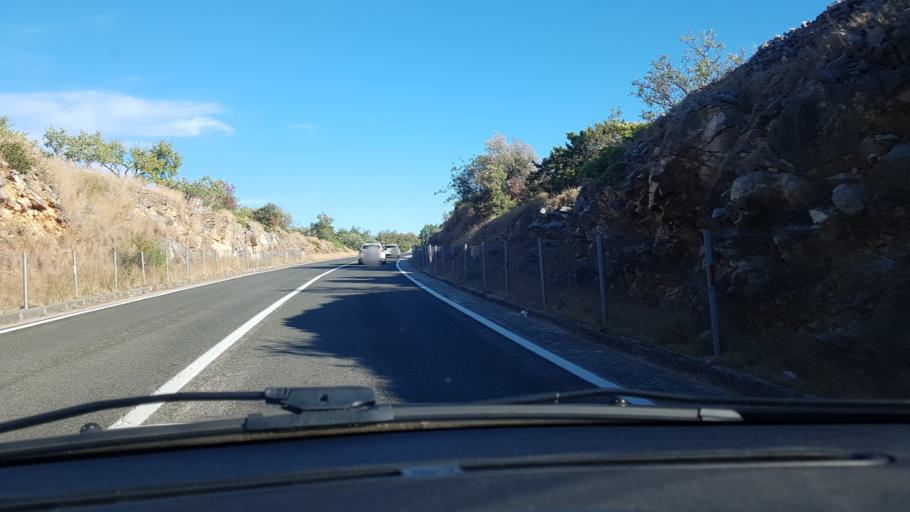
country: HR
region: Sibensko-Kniniska
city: Primosten
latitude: 43.5801
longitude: 15.9375
